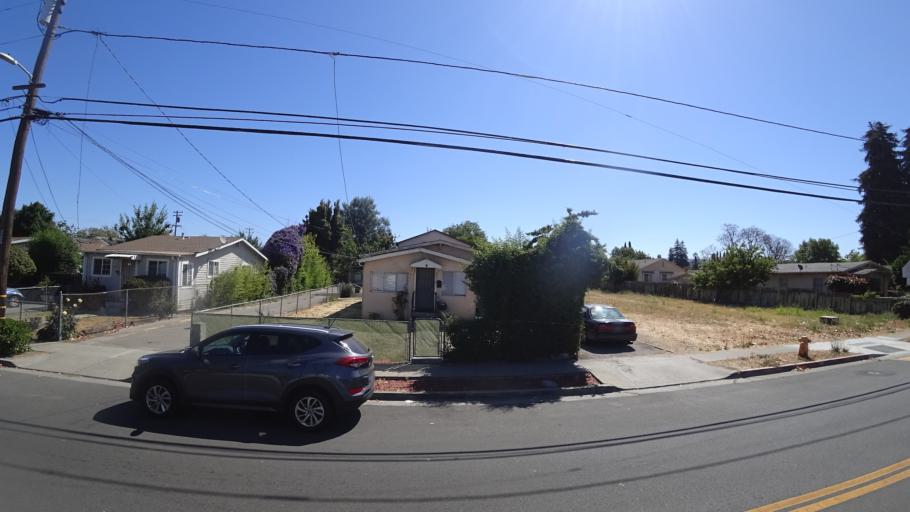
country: US
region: California
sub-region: Alameda County
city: Hayward
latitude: 37.6662
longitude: -122.0944
